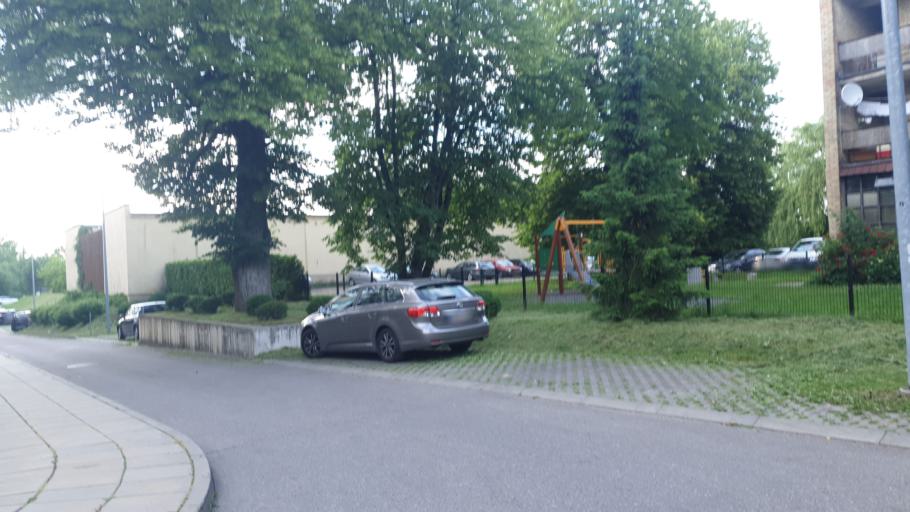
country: LT
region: Vilnius County
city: Rasos
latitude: 54.7261
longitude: 25.3228
